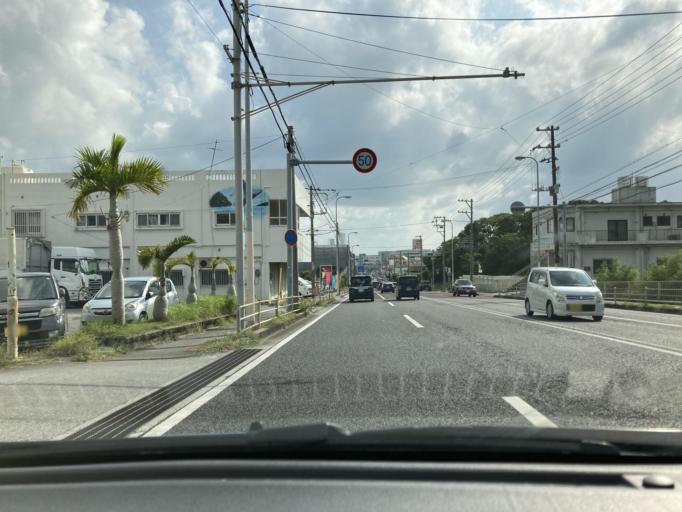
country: JP
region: Okinawa
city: Ginowan
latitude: 26.2298
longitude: 127.7683
